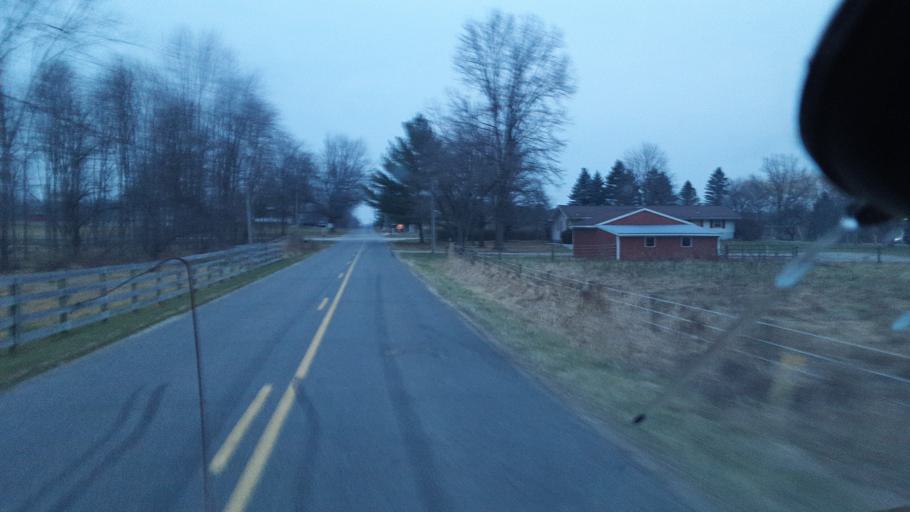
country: US
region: Indiana
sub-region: Elkhart County
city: Bristol
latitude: 41.6663
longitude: -85.7873
